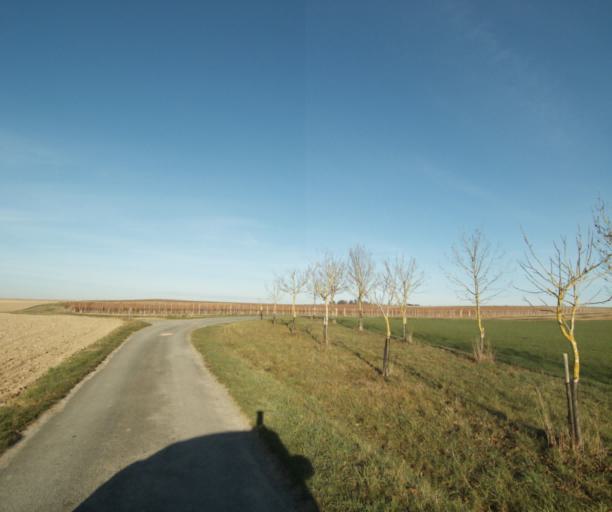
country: FR
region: Poitou-Charentes
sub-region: Departement de la Charente-Maritime
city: Cherac
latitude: 45.6935
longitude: -0.4582
